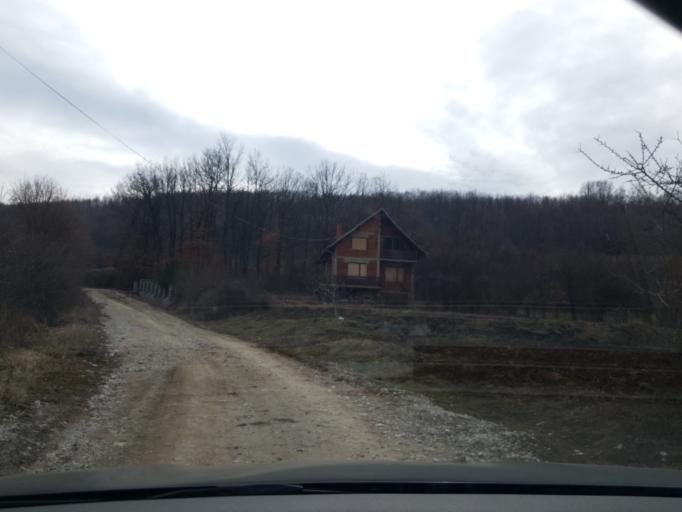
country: RS
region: Central Serbia
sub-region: Pirotski Okrug
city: Dimitrovgrad
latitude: 43.0069
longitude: 22.7503
